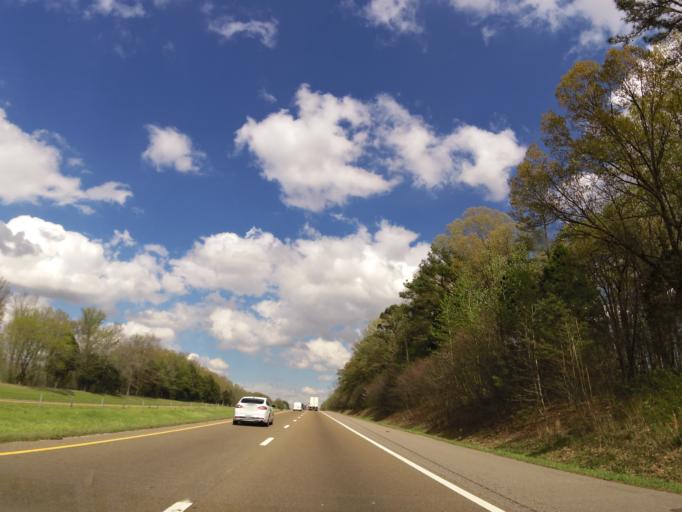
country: US
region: Tennessee
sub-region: Crockett County
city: Bells
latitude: 35.6197
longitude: -88.9916
